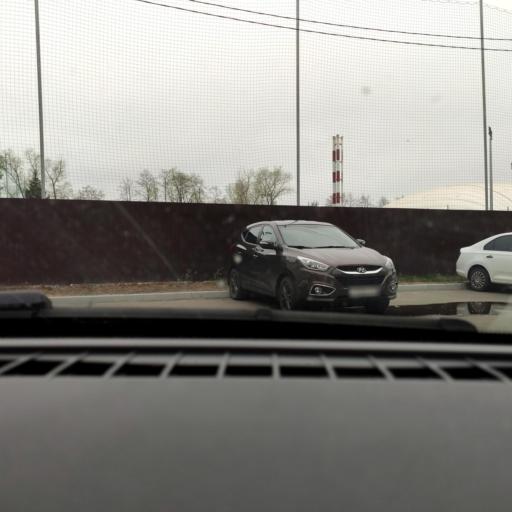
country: RU
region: Voronezj
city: Voronezh
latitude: 51.6664
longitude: 39.2793
